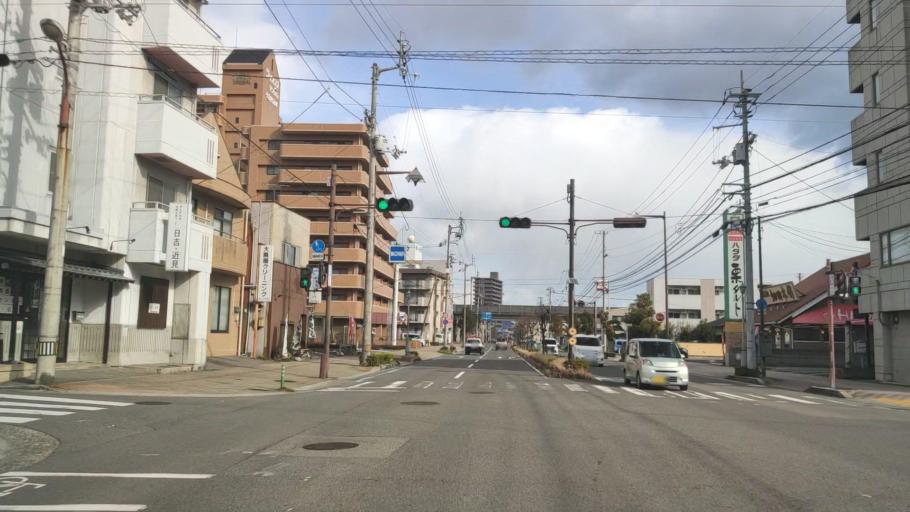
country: JP
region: Ehime
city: Hojo
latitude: 34.0655
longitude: 132.9900
